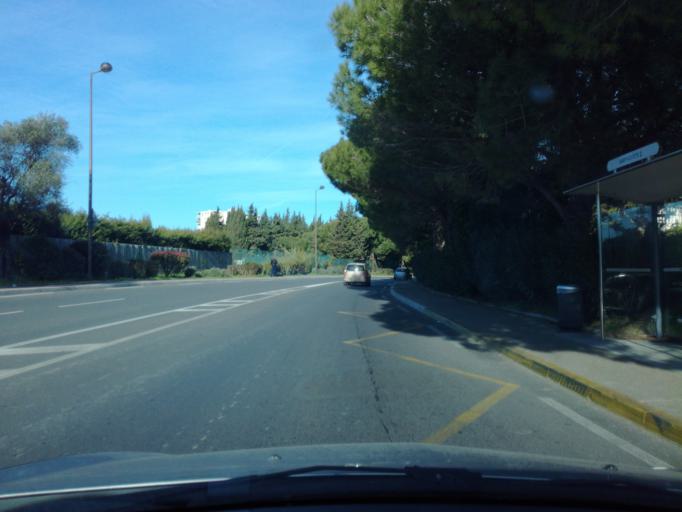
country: FR
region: Provence-Alpes-Cote d'Azur
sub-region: Departement des Alpes-Maritimes
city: Vallauris
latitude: 43.5746
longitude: 7.0905
